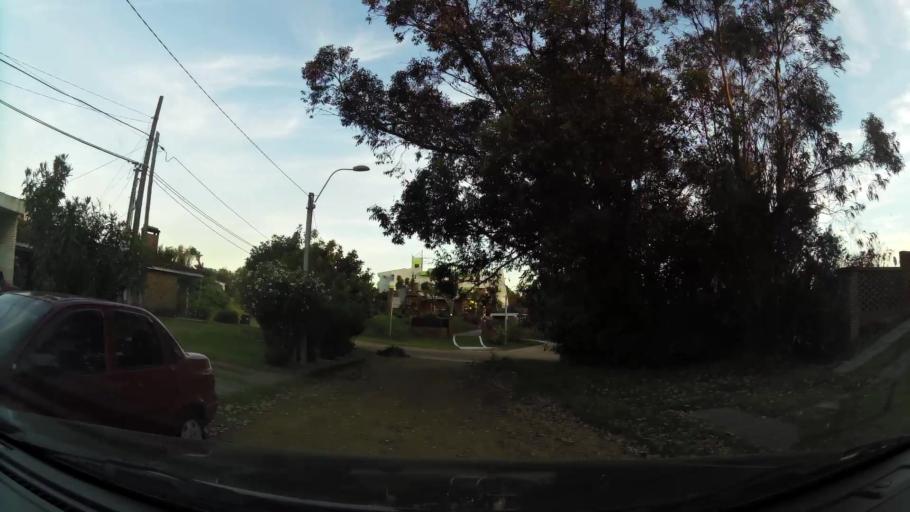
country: UY
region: Canelones
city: Atlantida
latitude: -34.7707
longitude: -55.7693
